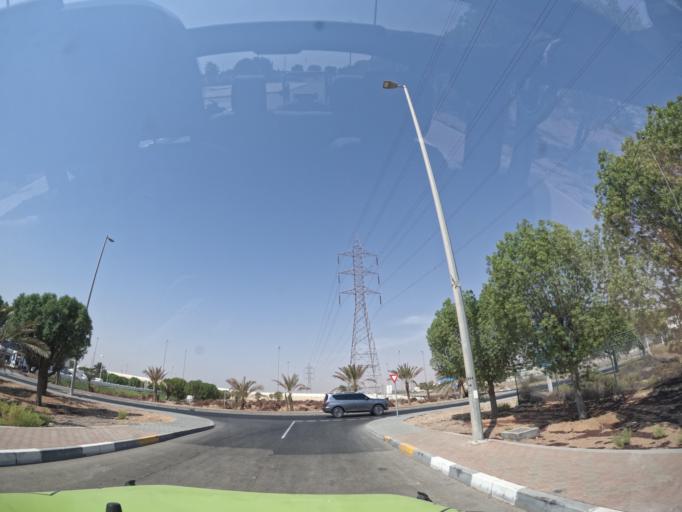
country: AE
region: Abu Dhabi
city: Al Ain
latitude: 24.2060
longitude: 55.3889
